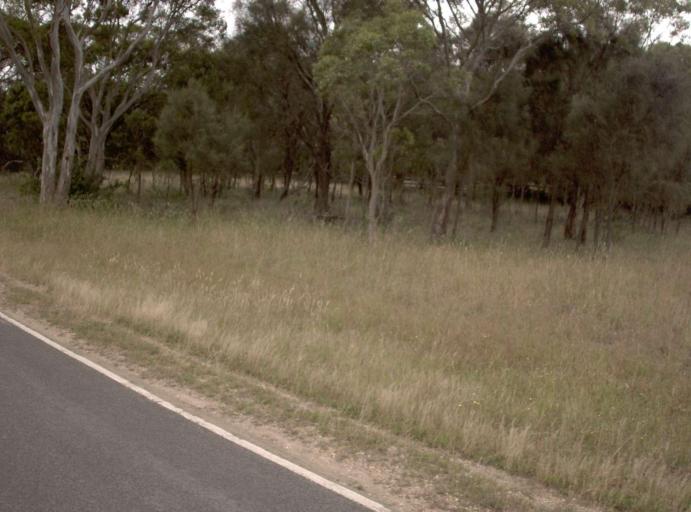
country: AU
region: Victoria
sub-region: Wellington
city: Heyfield
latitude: -38.0555
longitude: 146.7686
